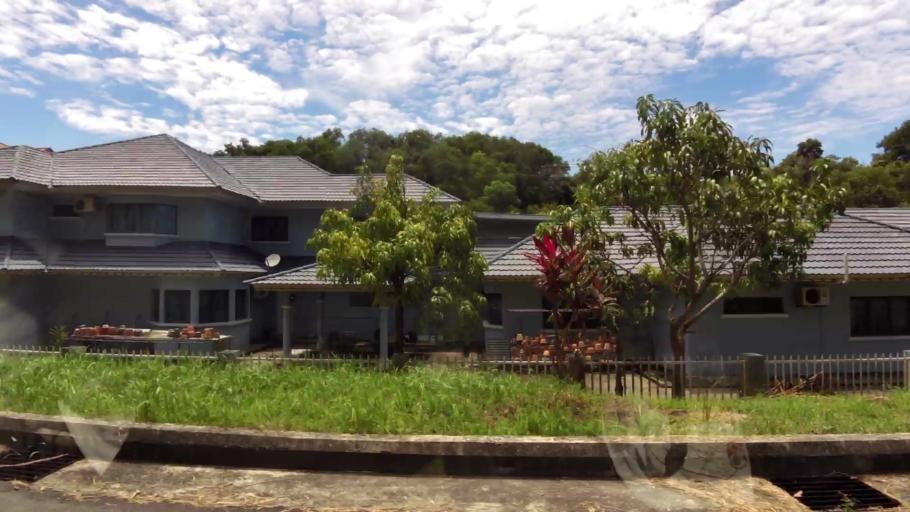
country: BN
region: Brunei and Muara
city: Bandar Seri Begawan
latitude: 4.9979
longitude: 115.0185
